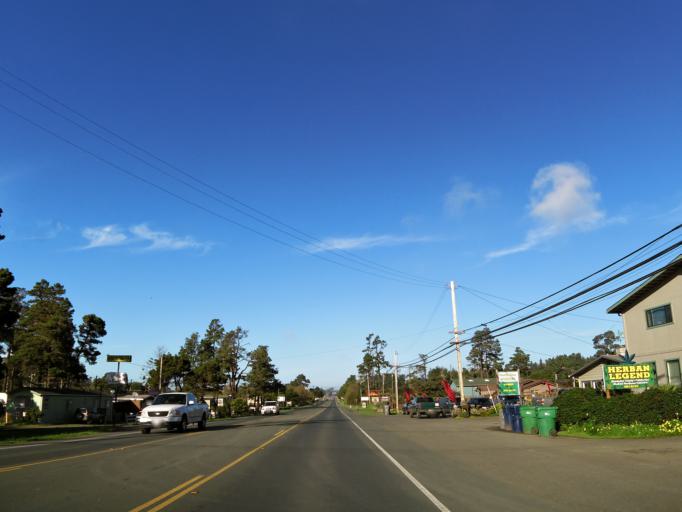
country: US
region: California
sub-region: Mendocino County
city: Fort Bragg
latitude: 39.4034
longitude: -123.8089
